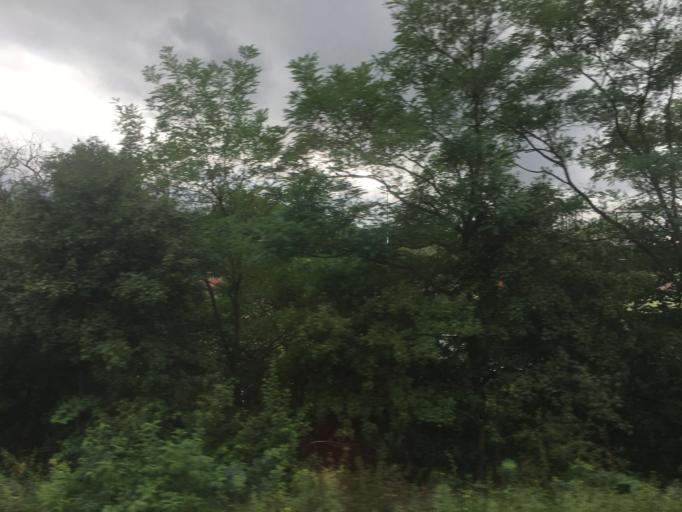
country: DE
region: Hesse
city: Niederrad
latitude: 50.0774
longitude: 8.6399
